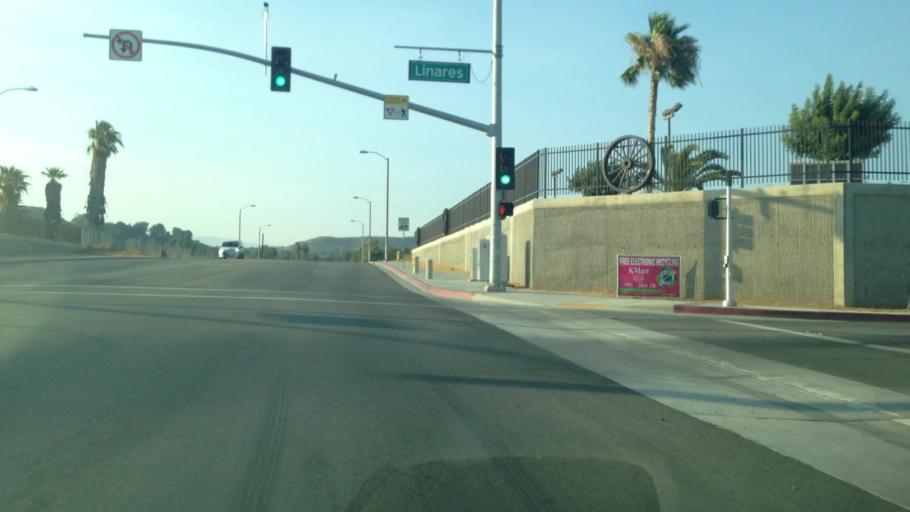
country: US
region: California
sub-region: Riverside County
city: Pedley
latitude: 33.9707
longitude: -117.4621
